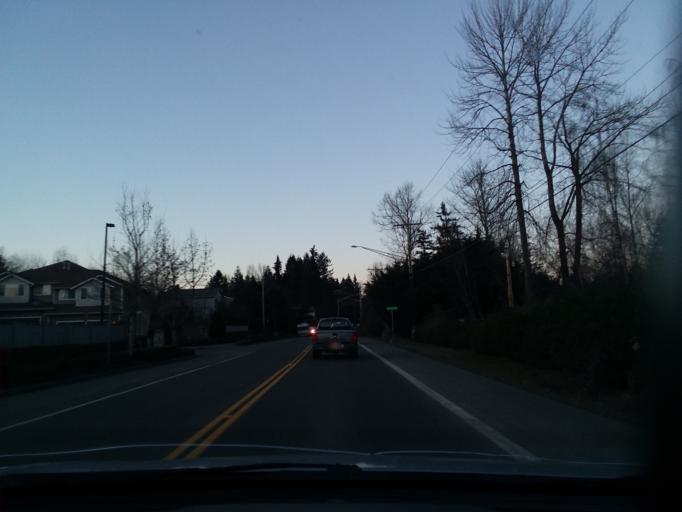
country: US
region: Washington
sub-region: Snohomish County
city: Martha Lake
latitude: 47.8693
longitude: -122.2671
